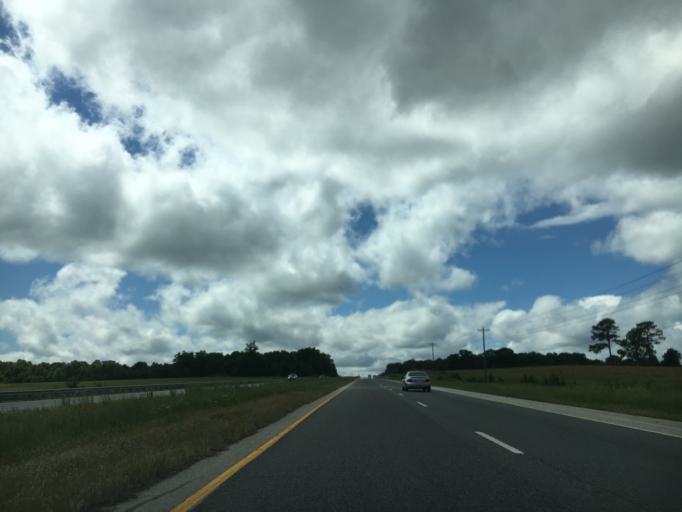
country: US
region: Virginia
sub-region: Mecklenburg County
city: Boydton
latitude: 36.6716
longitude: -78.2766
